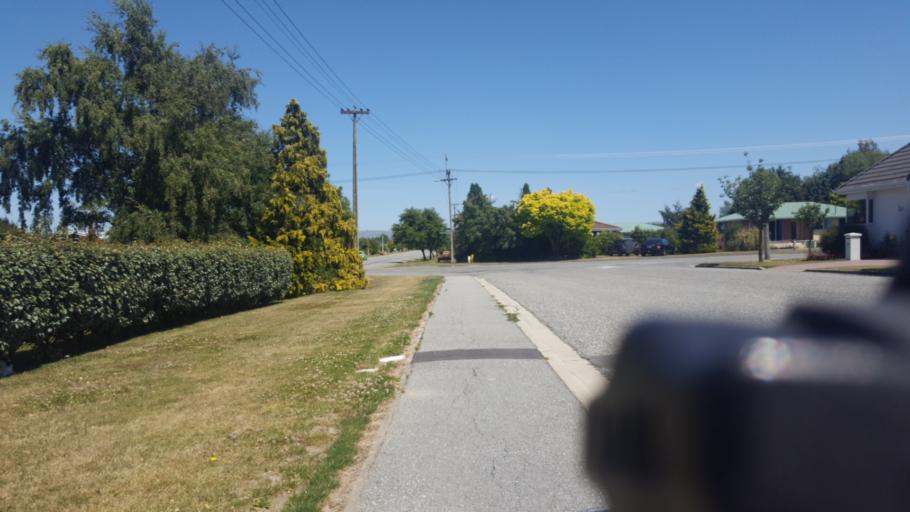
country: NZ
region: Otago
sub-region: Dunedin City
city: Dunedin
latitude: -45.1268
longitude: 170.1067
